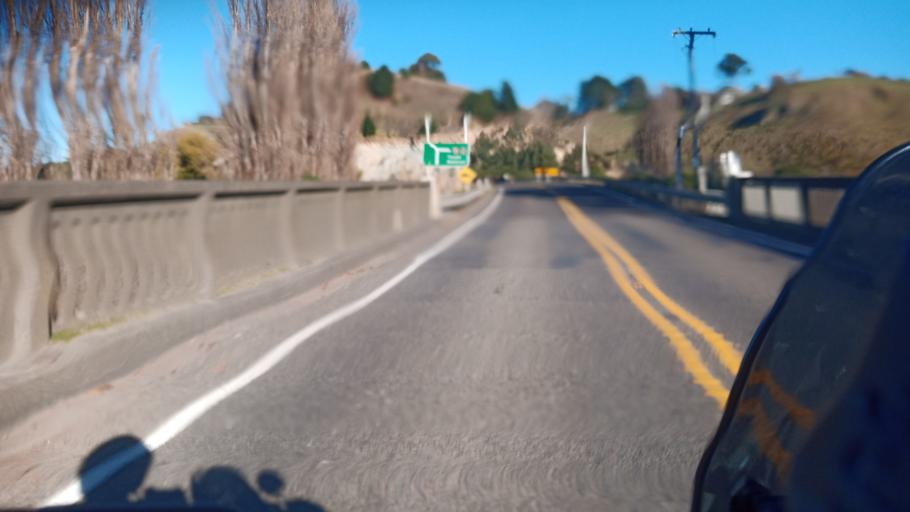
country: NZ
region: Hawke's Bay
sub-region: Napier City
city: Napier
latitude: -39.3942
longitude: 176.8773
